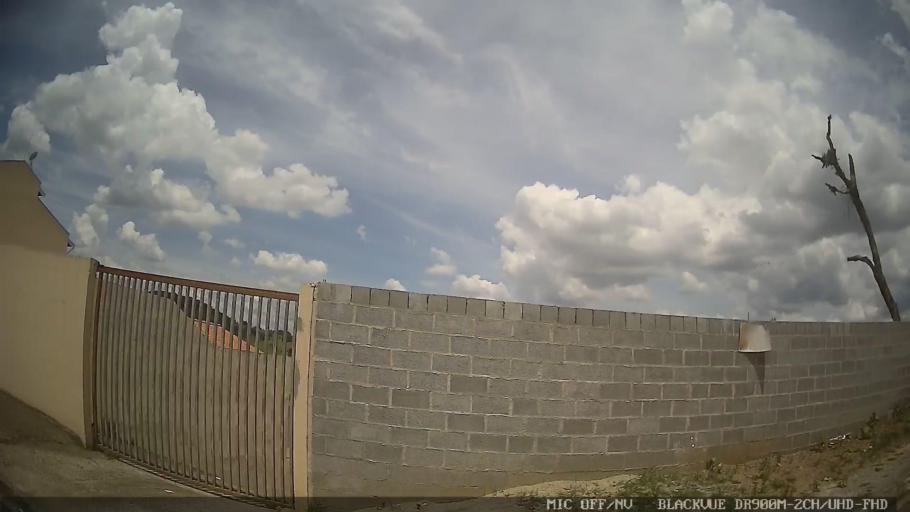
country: BR
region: Sao Paulo
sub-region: Atibaia
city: Atibaia
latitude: -23.0977
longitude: -46.5387
